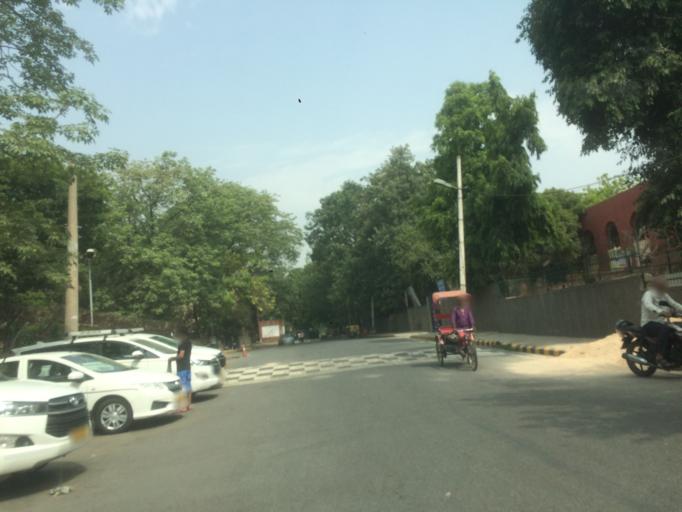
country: IN
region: NCT
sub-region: New Delhi
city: New Delhi
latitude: 28.6379
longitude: 77.2057
